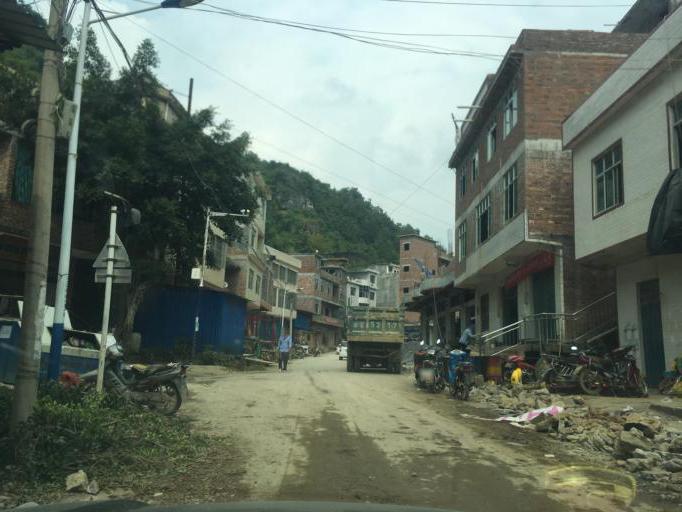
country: CN
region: Guangxi Zhuangzu Zizhiqu
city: Tongle
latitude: 25.3295
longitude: 105.9873
